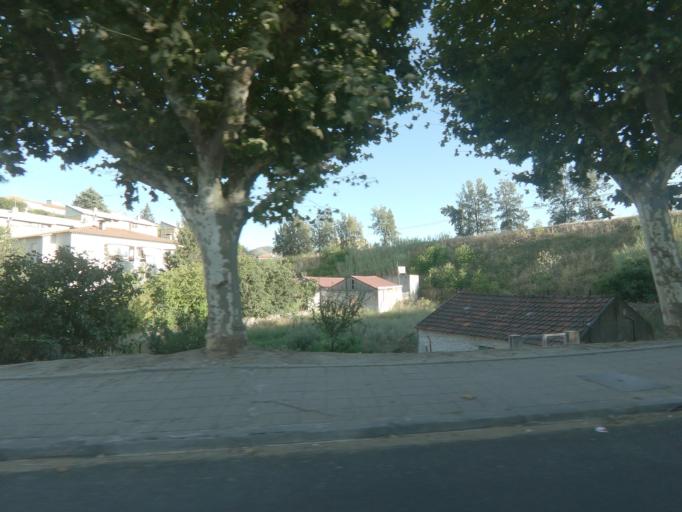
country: PT
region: Vila Real
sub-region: Peso da Regua
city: Peso da Regua
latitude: 41.1665
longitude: -7.7948
